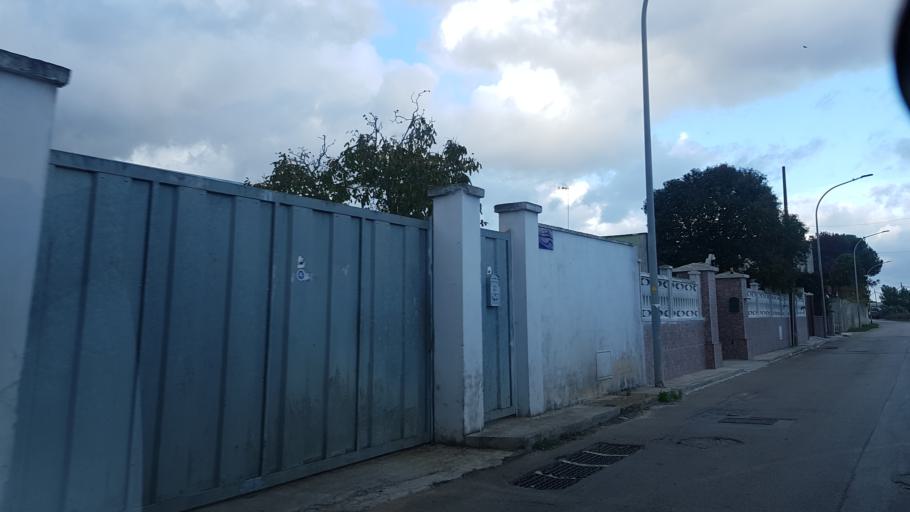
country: IT
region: Apulia
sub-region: Provincia di Brindisi
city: San Pietro Vernotico
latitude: 40.4928
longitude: 18.0005
